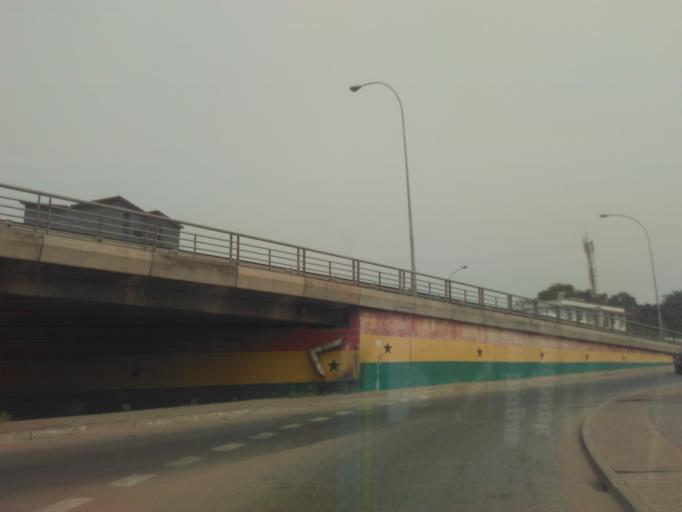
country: GH
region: Greater Accra
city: Accra
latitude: 5.5741
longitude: -0.1983
